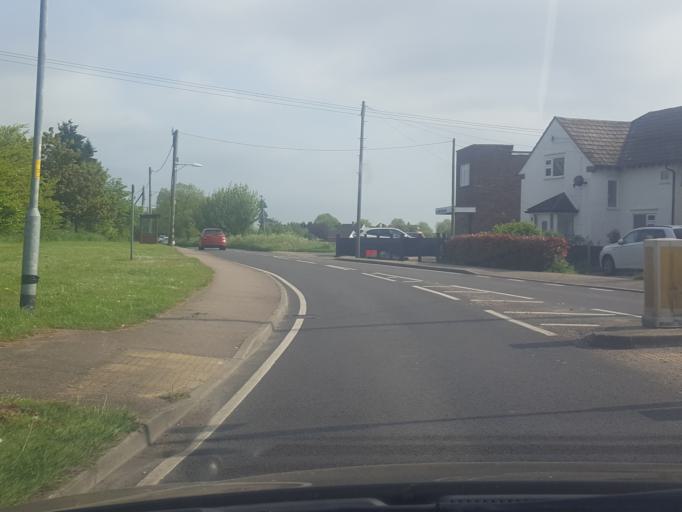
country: GB
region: England
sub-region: Essex
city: Frinton-on-Sea
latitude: 51.8322
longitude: 1.2093
